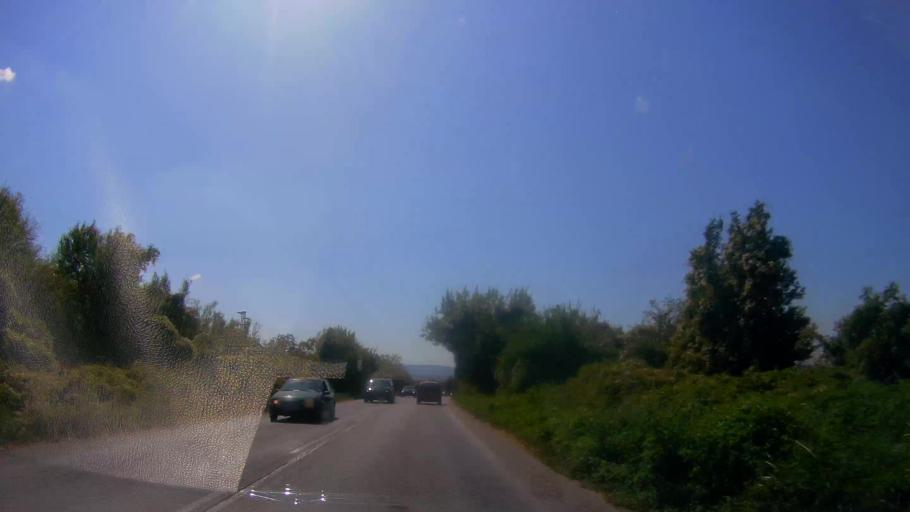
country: BG
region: Veliko Turnovo
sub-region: Obshtina Gorna Oryakhovitsa
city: Purvomaytsi
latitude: 43.2316
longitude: 25.6402
